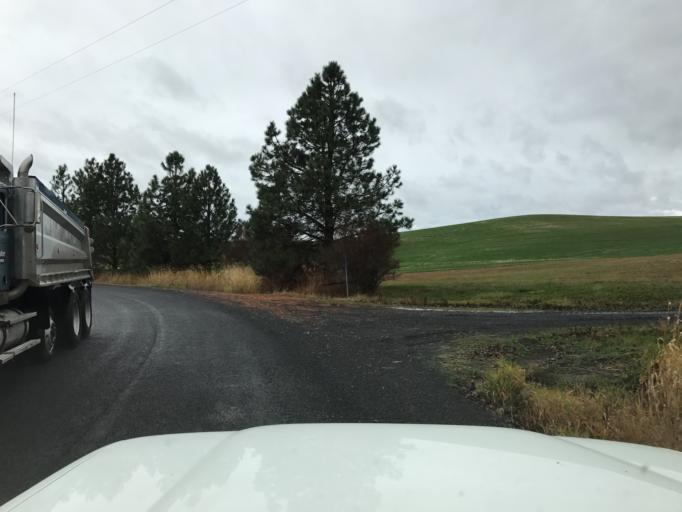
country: US
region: Idaho
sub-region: Latah County
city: Moscow
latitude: 46.7912
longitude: -116.9645
